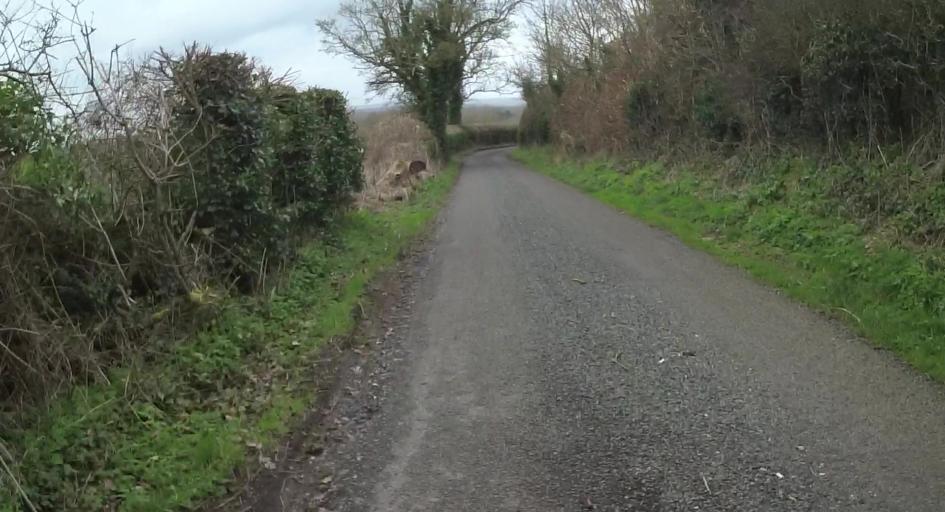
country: GB
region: England
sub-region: Hampshire
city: Kingsclere
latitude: 51.3145
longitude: -1.2225
